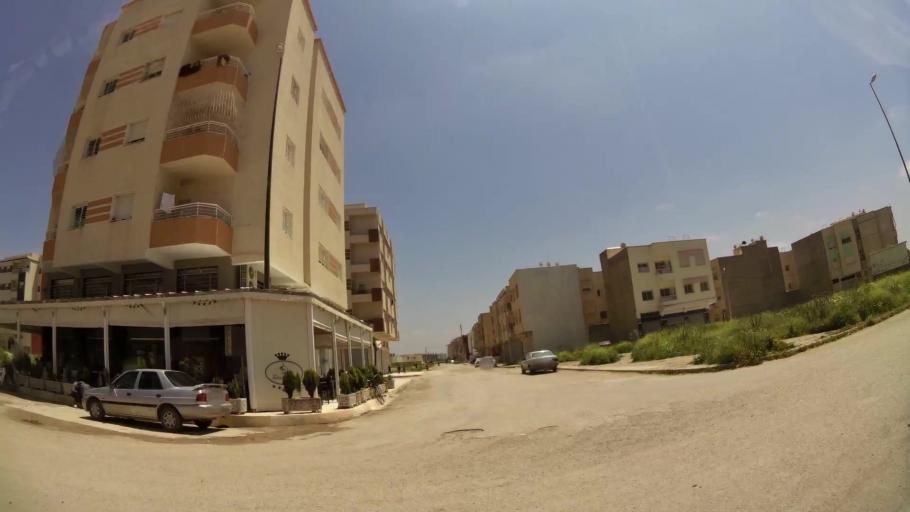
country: MA
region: Fes-Boulemane
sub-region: Fes
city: Fes
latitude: 34.0280
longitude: -5.0453
